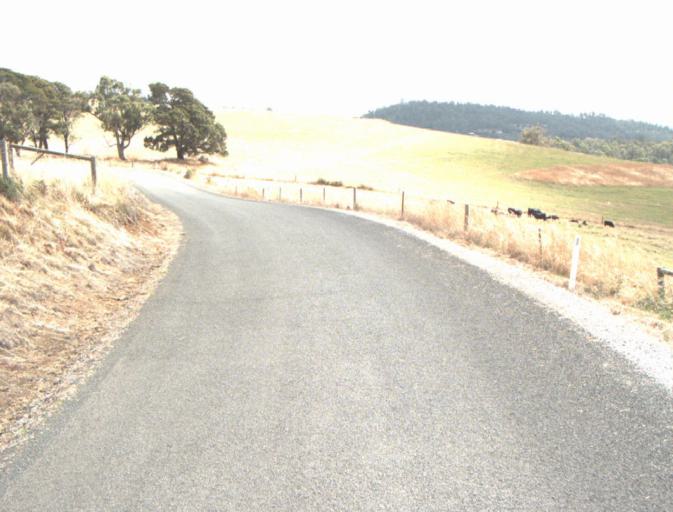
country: AU
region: Tasmania
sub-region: Launceston
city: Mayfield
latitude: -41.3082
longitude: 146.9959
